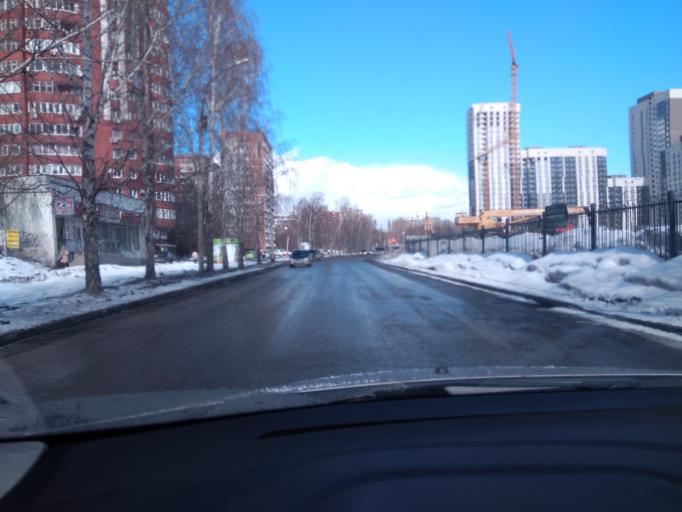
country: RU
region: Sverdlovsk
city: Sovkhoznyy
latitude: 56.8118
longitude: 60.5669
